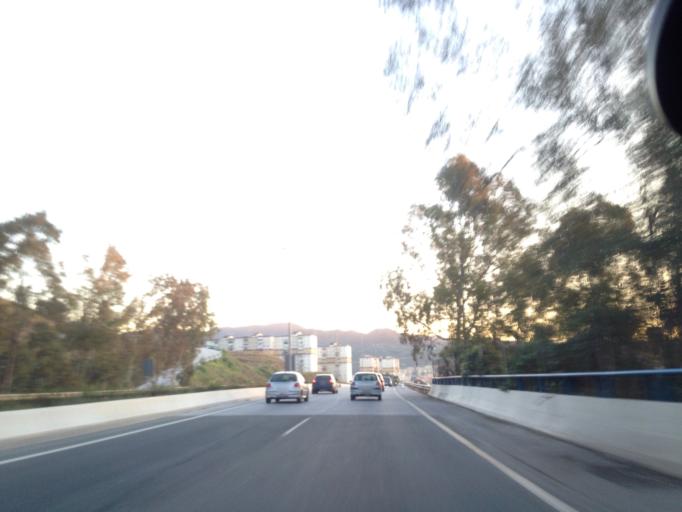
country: ES
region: Andalusia
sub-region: Provincia de Malaga
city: Malaga
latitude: 36.7342
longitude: -4.4376
